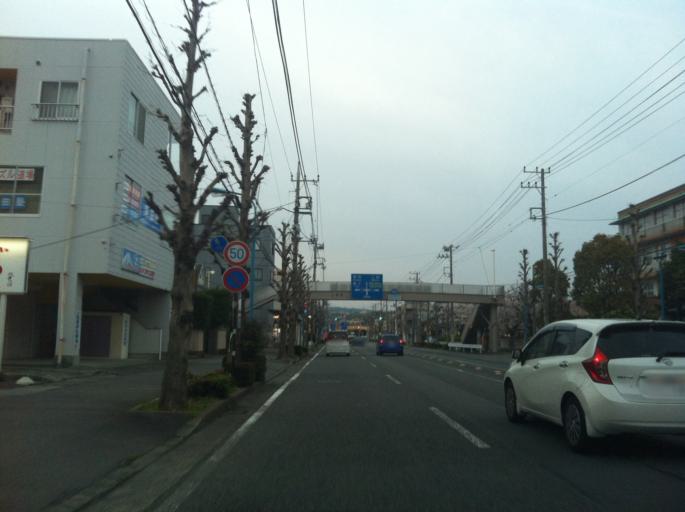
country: JP
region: Shizuoka
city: Numazu
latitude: 35.1189
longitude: 138.8602
